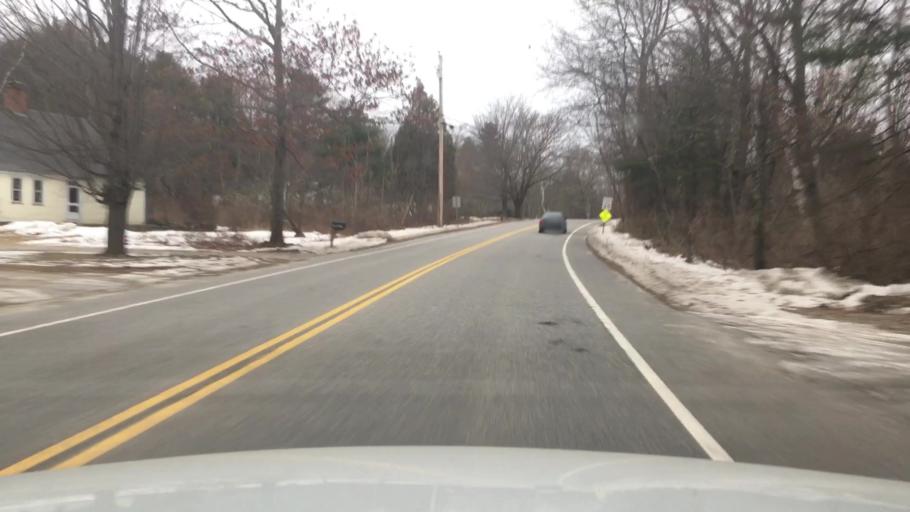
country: US
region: Maine
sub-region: Cumberland County
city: Freeport
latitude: 43.8731
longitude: -70.0643
